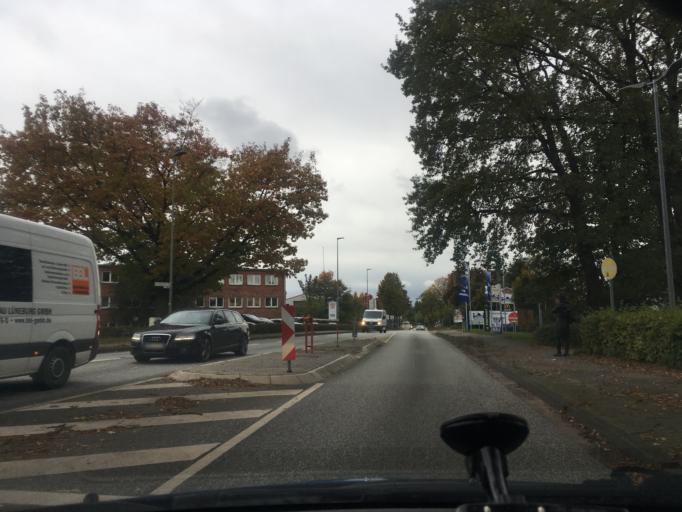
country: DE
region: Schleswig-Holstein
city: Geesthacht
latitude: 53.4330
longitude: 10.3546
